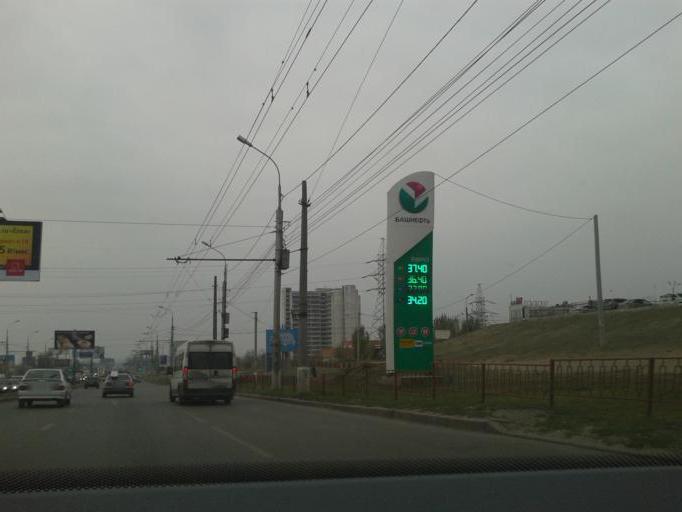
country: RU
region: Volgograd
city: Volgograd
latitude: 48.6450
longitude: 44.4331
